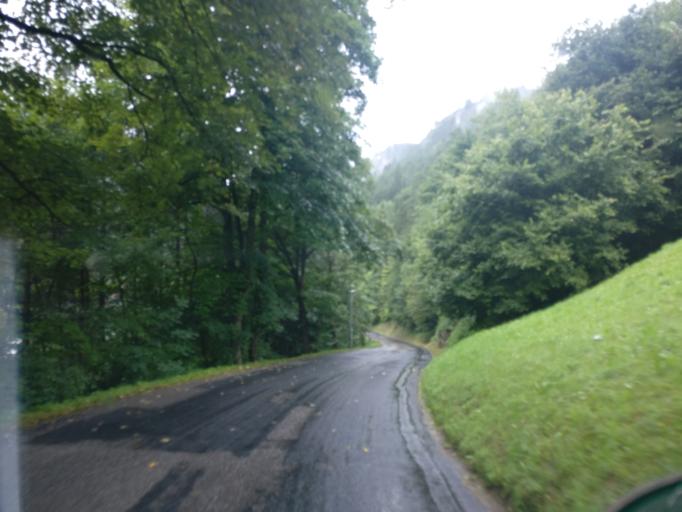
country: AT
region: Lower Austria
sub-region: Politischer Bezirk Neunkirchen
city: Semmering
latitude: 47.6579
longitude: 15.8217
